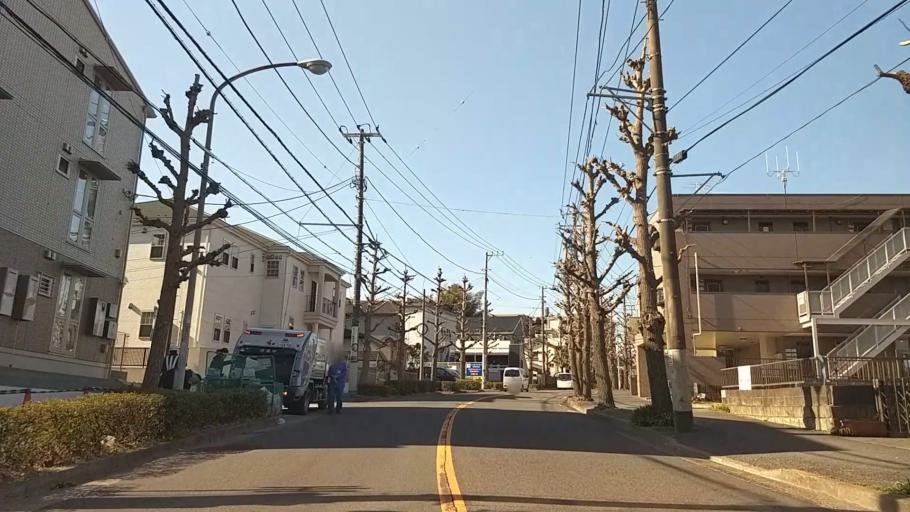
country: JP
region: Kanagawa
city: Yokohama
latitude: 35.3853
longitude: 139.6004
